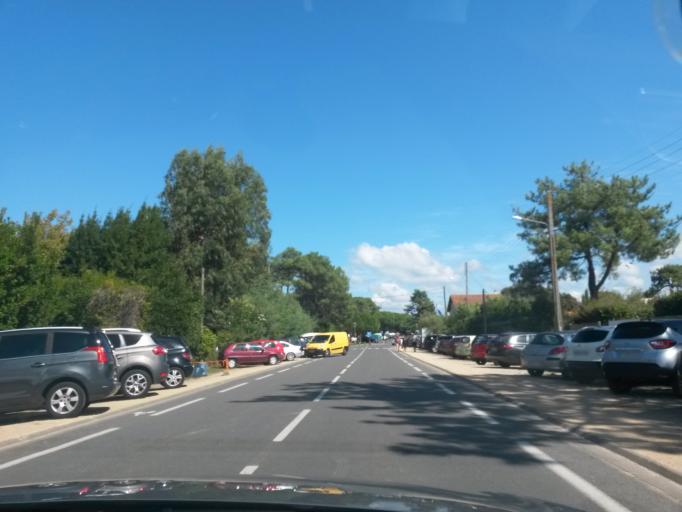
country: FR
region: Aquitaine
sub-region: Departement de la Gironde
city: Arcachon
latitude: 44.6565
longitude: -1.2432
